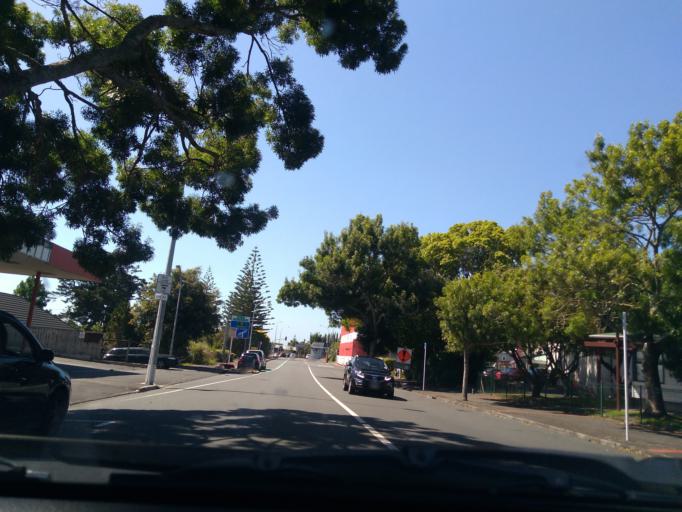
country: NZ
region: Auckland
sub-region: Auckland
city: Rosebank
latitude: -36.8938
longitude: 174.6964
